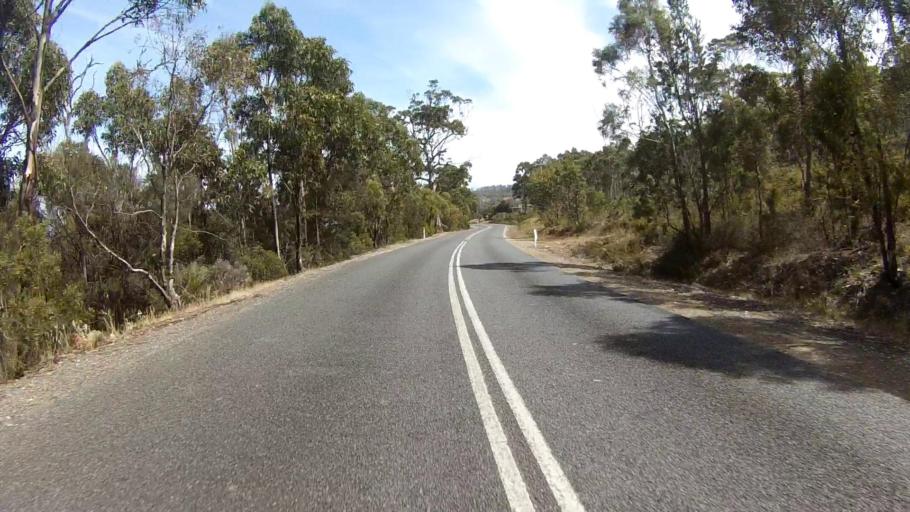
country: AU
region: Tasmania
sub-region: Huon Valley
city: Cygnet
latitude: -43.2818
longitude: 147.1674
